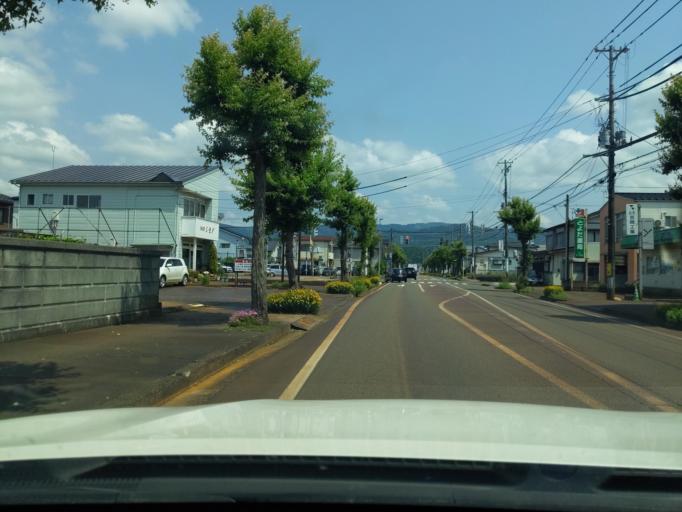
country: JP
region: Niigata
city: Nagaoka
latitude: 37.4297
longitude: 138.8553
